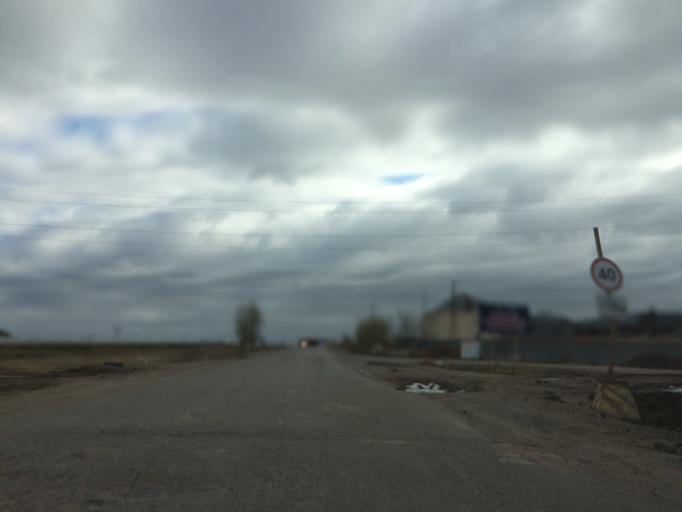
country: KZ
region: Astana Qalasy
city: Astana
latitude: 51.2080
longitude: 71.4496
